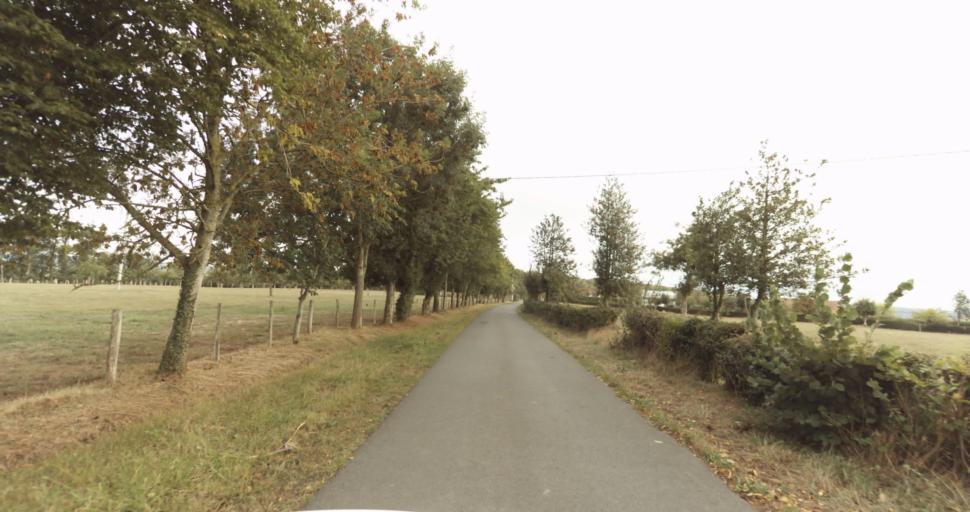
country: FR
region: Lower Normandy
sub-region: Departement de l'Orne
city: Vimoutiers
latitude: 48.9273
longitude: 0.1486
